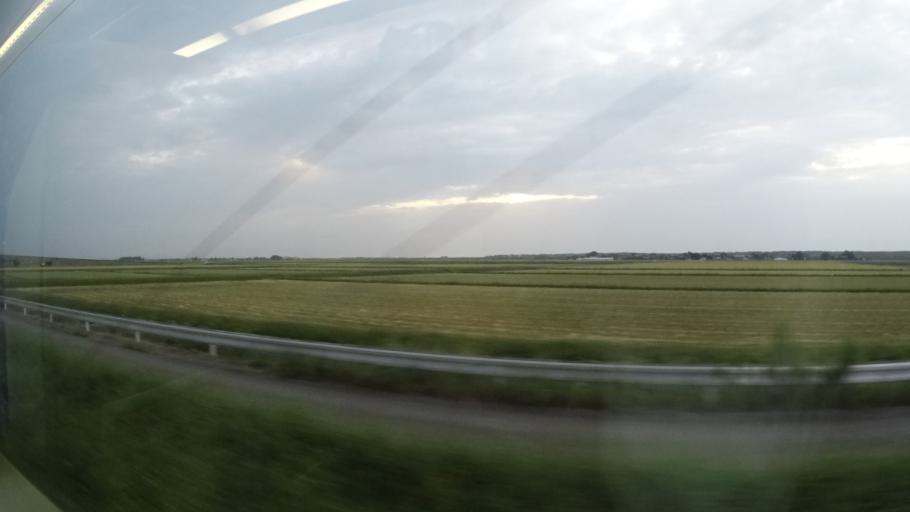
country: JP
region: Niigata
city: Murakami
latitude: 38.1658
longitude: 139.4593
